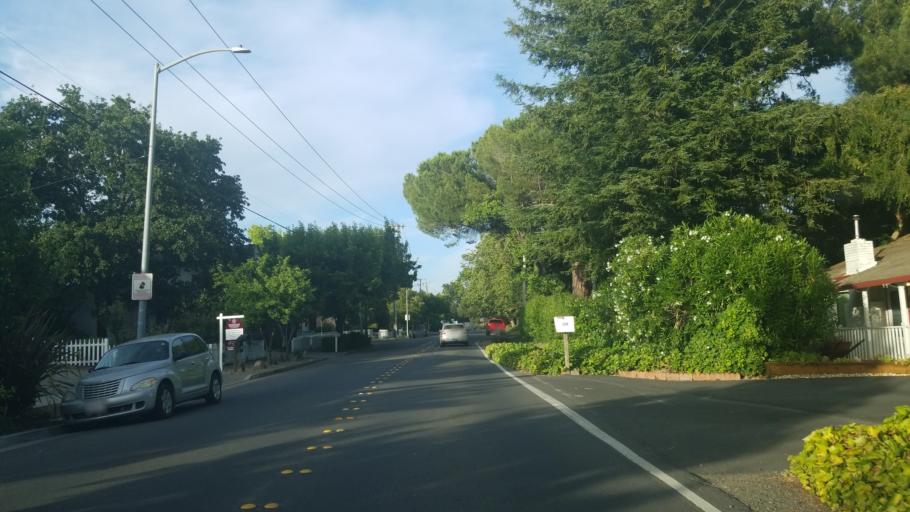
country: US
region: California
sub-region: Sonoma County
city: Santa Rosa
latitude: 38.4515
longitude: -122.7372
